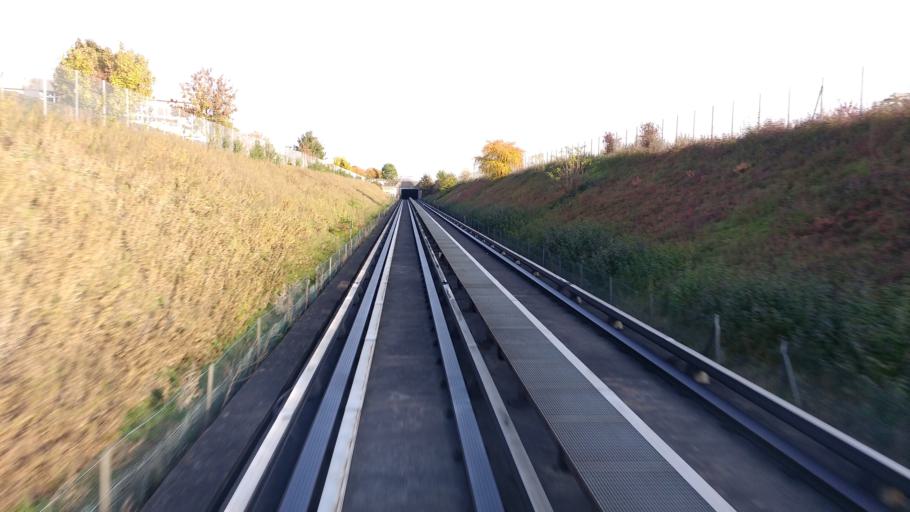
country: FR
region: Ile-de-France
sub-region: Departement du Val-de-Marne
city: Rungis
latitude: 48.7378
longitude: 2.3535
